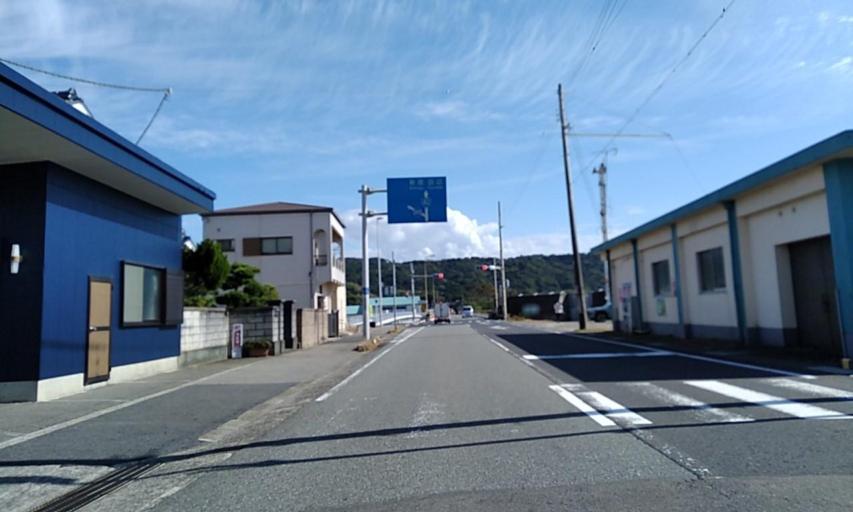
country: JP
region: Wakayama
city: Gobo
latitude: 33.8001
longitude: 135.2347
